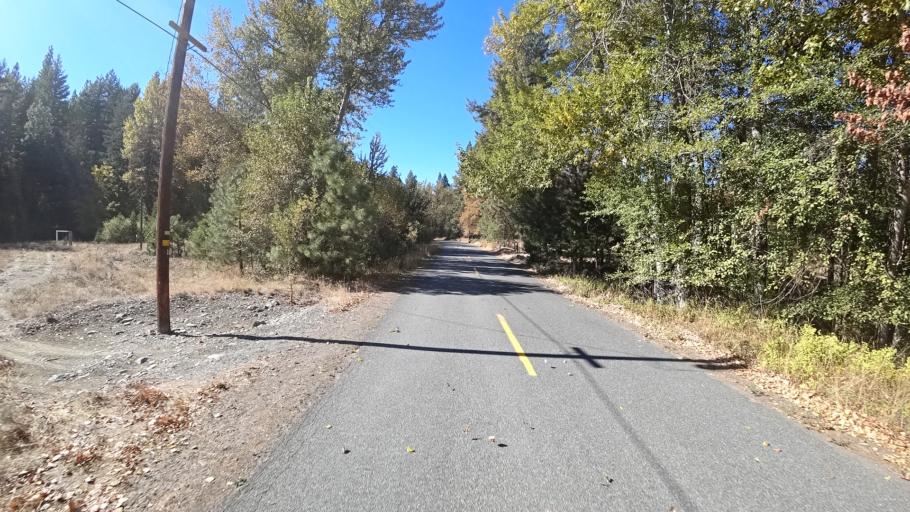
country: US
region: California
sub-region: Siskiyou County
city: Yreka
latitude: 41.5333
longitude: -122.9415
